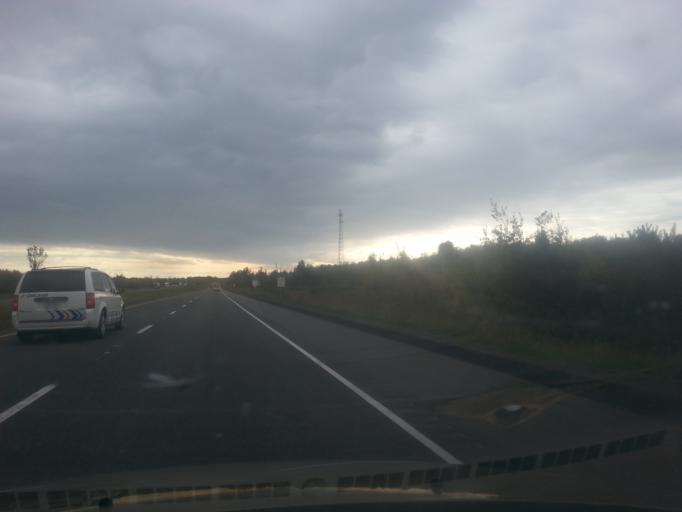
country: CA
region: Ontario
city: Quinte West
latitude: 44.0695
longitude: -77.7761
